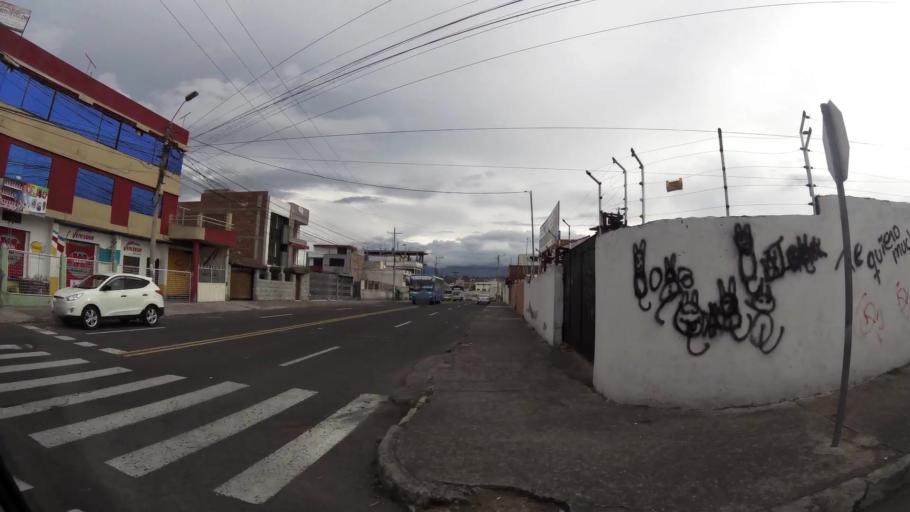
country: EC
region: Tungurahua
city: Ambato
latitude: -1.2734
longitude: -78.6268
